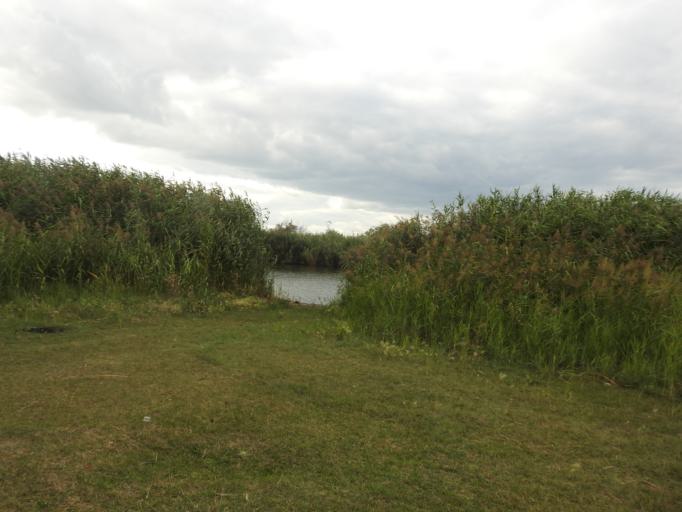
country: RU
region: Saratov
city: Shumeyka
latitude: 51.4190
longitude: 46.3067
